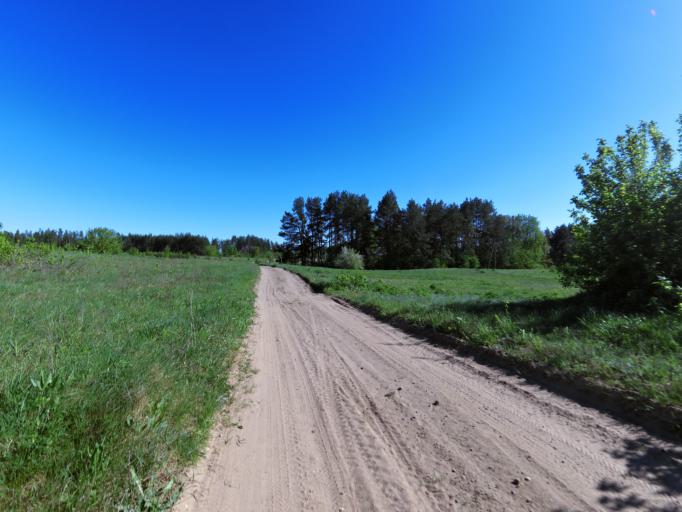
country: LT
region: Vilnius County
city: Pilaite
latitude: 54.6850
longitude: 25.1612
